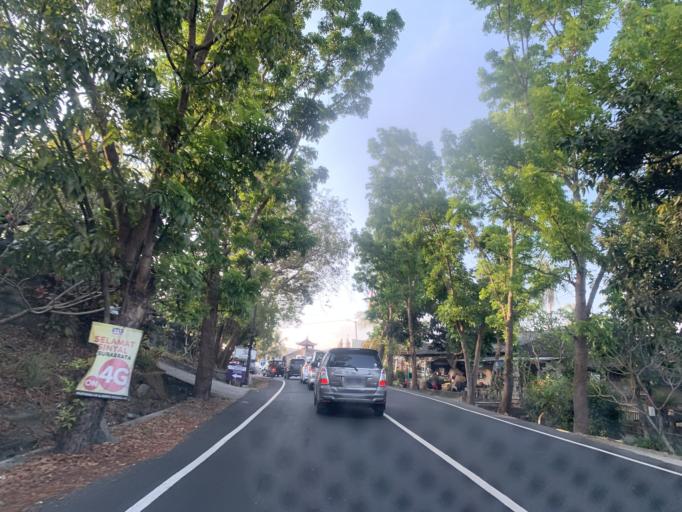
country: ID
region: Bali
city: Banjar Delodrurung
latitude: -8.4958
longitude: 114.9664
